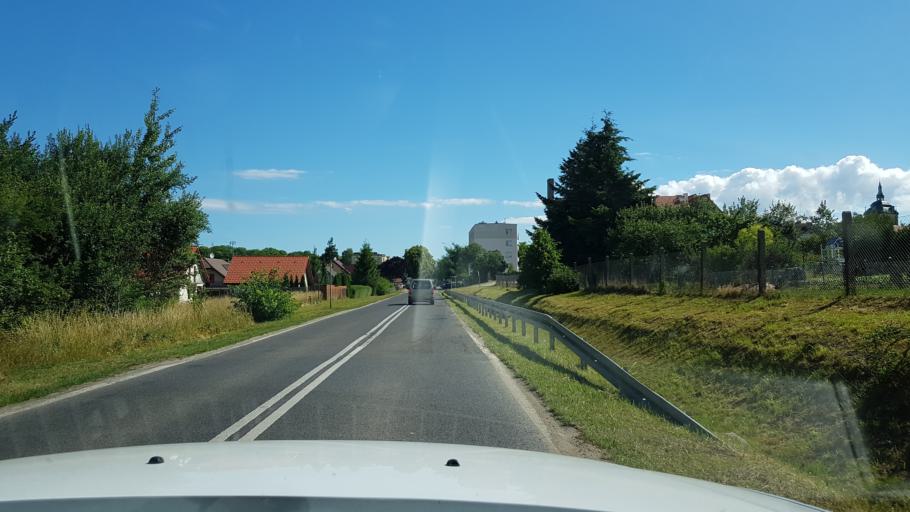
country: PL
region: West Pomeranian Voivodeship
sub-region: Powiat gryficki
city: Trzebiatow
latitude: 54.0530
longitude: 15.2531
